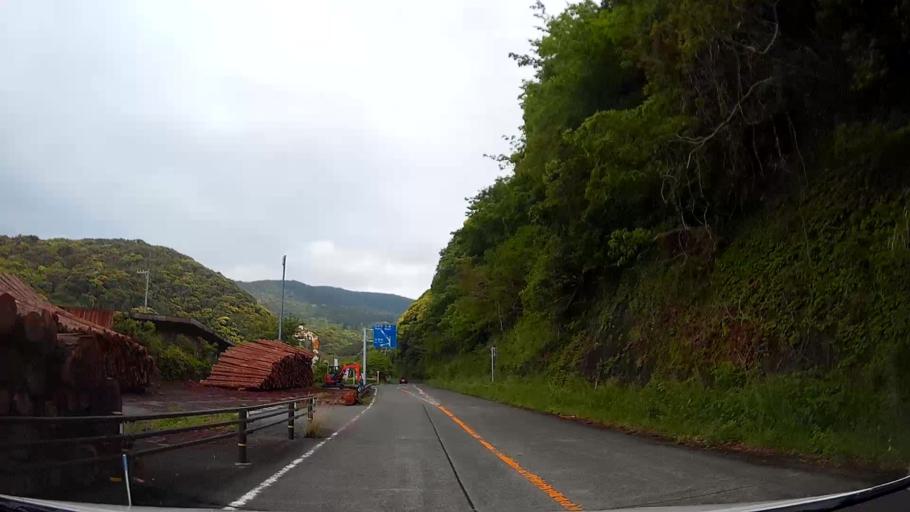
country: JP
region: Shizuoka
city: Shimoda
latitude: 34.6981
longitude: 138.7596
